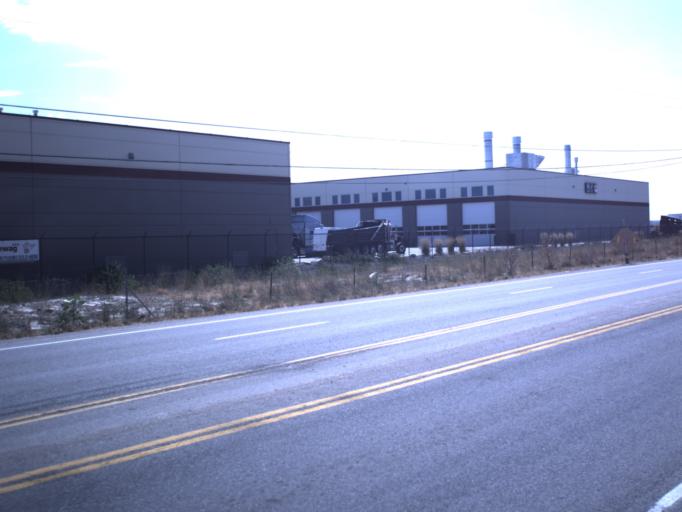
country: US
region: Utah
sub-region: Salt Lake County
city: West Valley City
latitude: 40.7302
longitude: -112.0250
